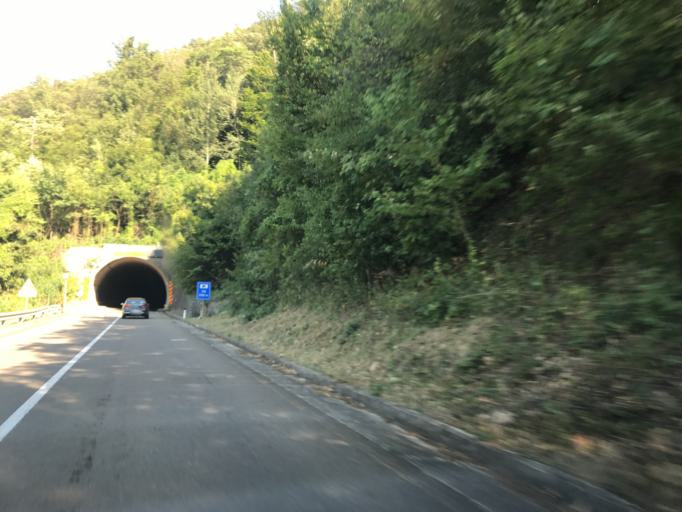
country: RO
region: Caras-Severin
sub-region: Comuna Berzasca
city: Berzasca
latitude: 44.5943
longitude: 22.0162
